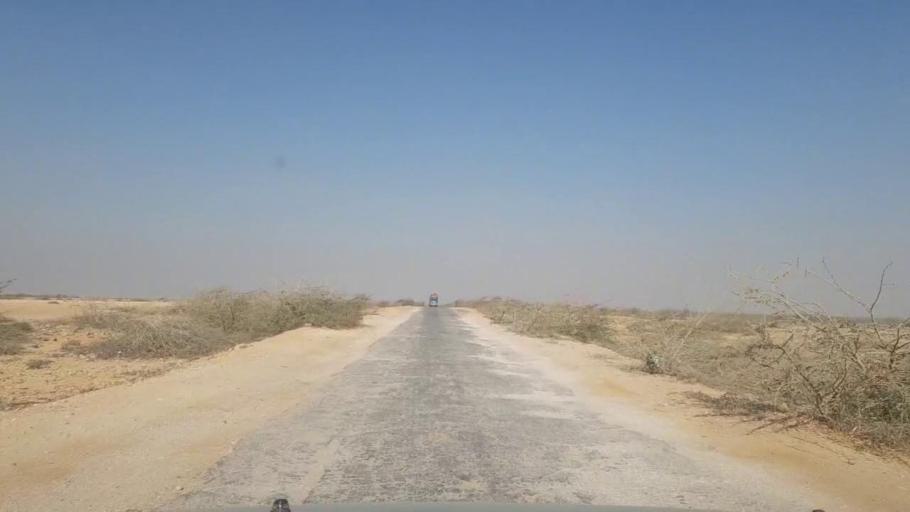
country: PK
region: Sindh
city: Thatta
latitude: 24.8365
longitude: 67.8897
